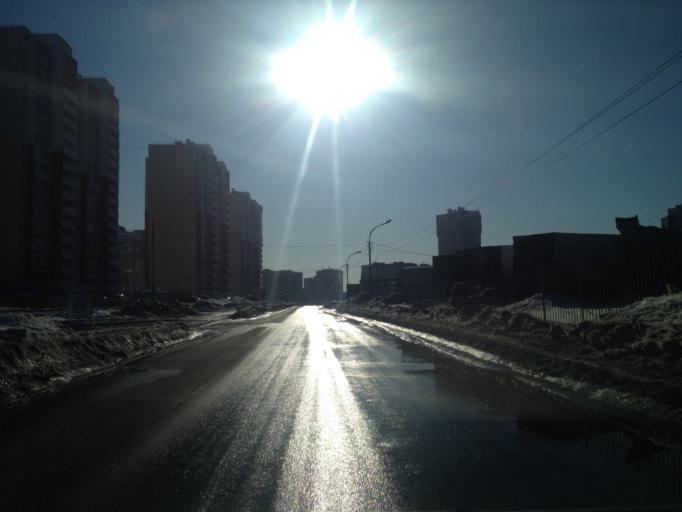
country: RU
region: Sverdlovsk
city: Yekaterinburg
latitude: 56.9106
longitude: 60.6254
